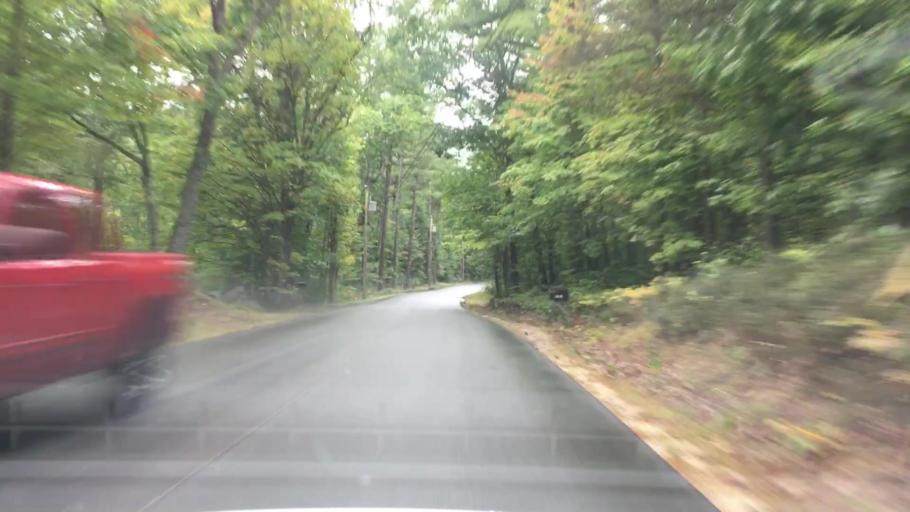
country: US
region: Maine
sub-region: Cumberland County
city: Raymond
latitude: 43.9895
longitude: -70.5640
